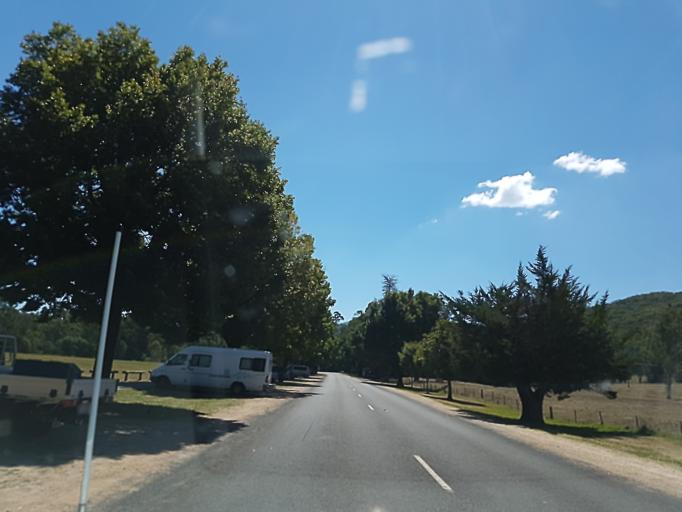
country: AU
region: Victoria
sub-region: Alpine
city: Mount Beauty
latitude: -36.7465
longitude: 146.9795
